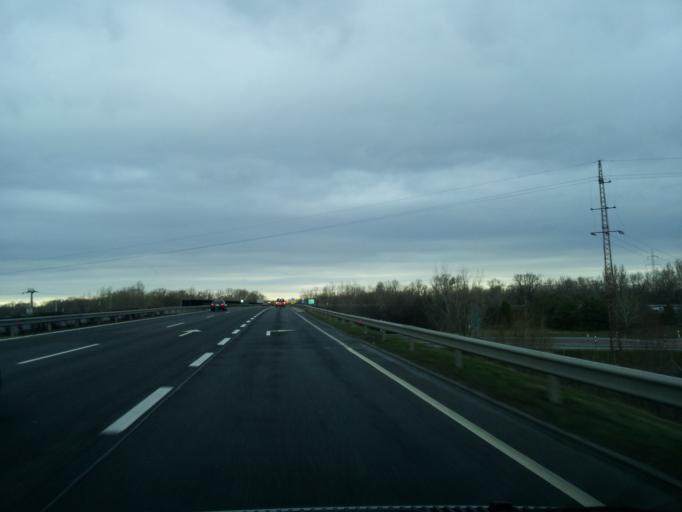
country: HU
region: Gyor-Moson-Sopron
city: Abda
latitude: 47.6763
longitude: 17.5511
